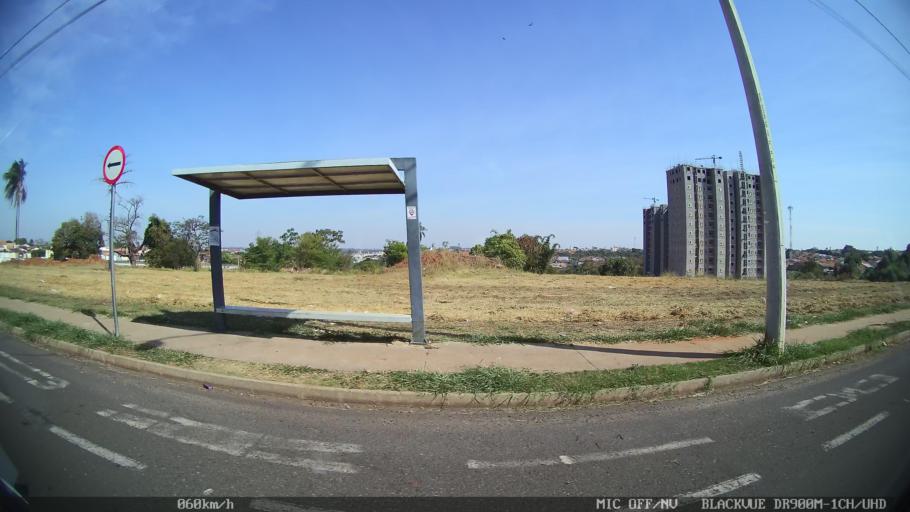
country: BR
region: Sao Paulo
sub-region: Sao Jose Do Rio Preto
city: Sao Jose do Rio Preto
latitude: -20.7892
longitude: -49.4224
